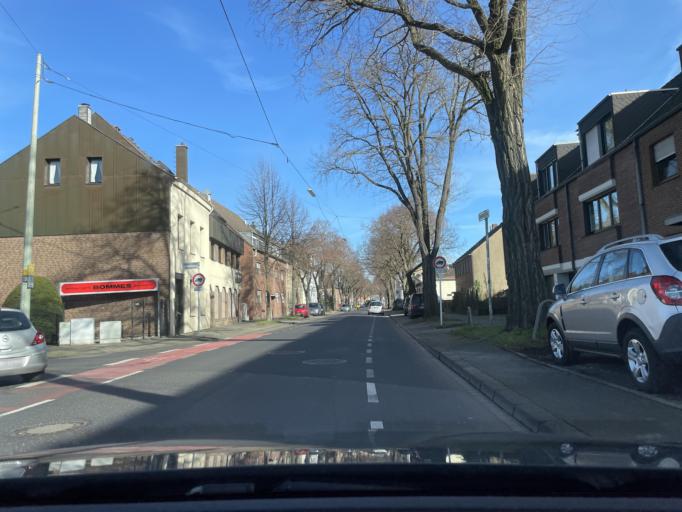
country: DE
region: North Rhine-Westphalia
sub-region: Regierungsbezirk Dusseldorf
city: Monchengladbach
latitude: 51.2138
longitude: 6.4649
